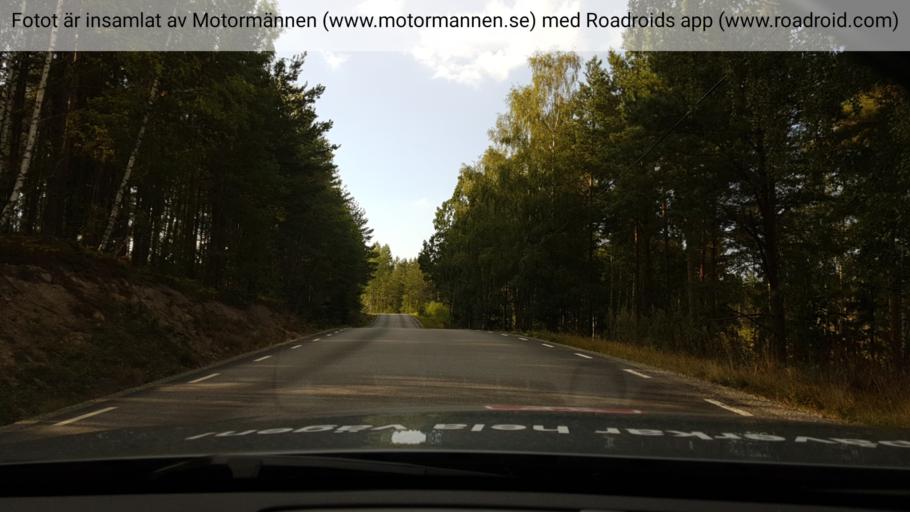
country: SE
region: Soedermanland
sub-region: Gnesta Kommun
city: Gnesta
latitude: 59.1170
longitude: 17.2200
